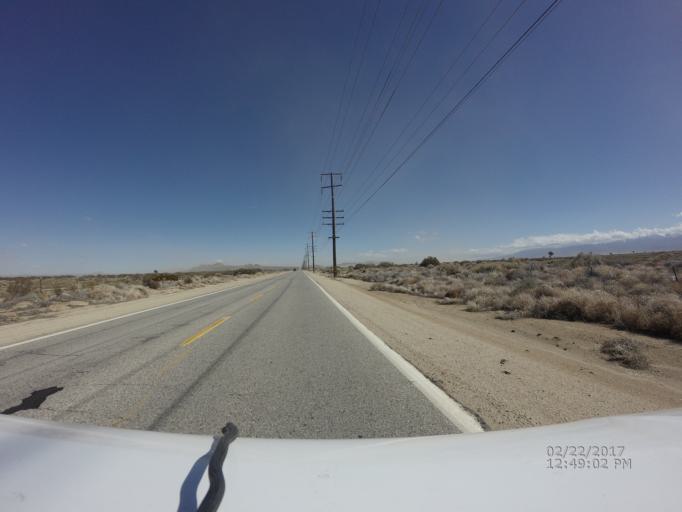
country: US
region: California
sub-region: Los Angeles County
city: Littlerock
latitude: 34.6166
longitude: -117.9604
